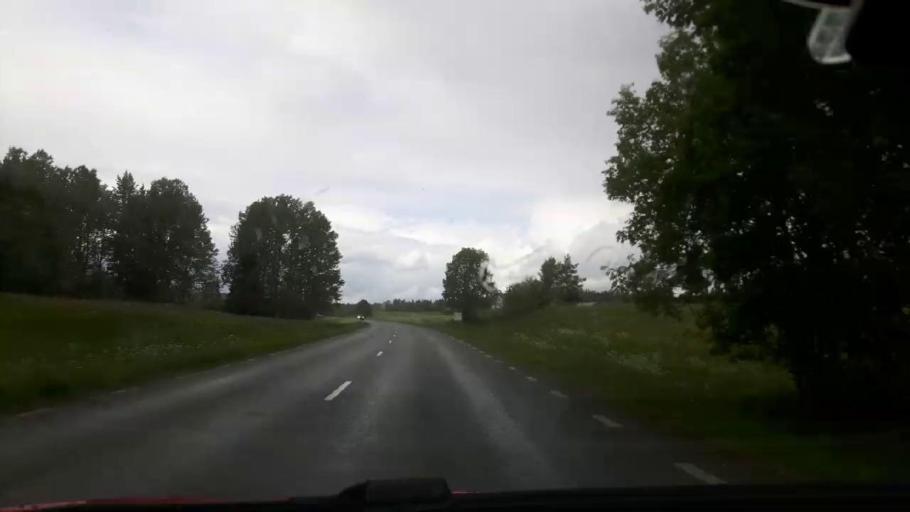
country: SE
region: Jaemtland
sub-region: Krokoms Kommun
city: Krokom
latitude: 63.4498
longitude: 14.1946
